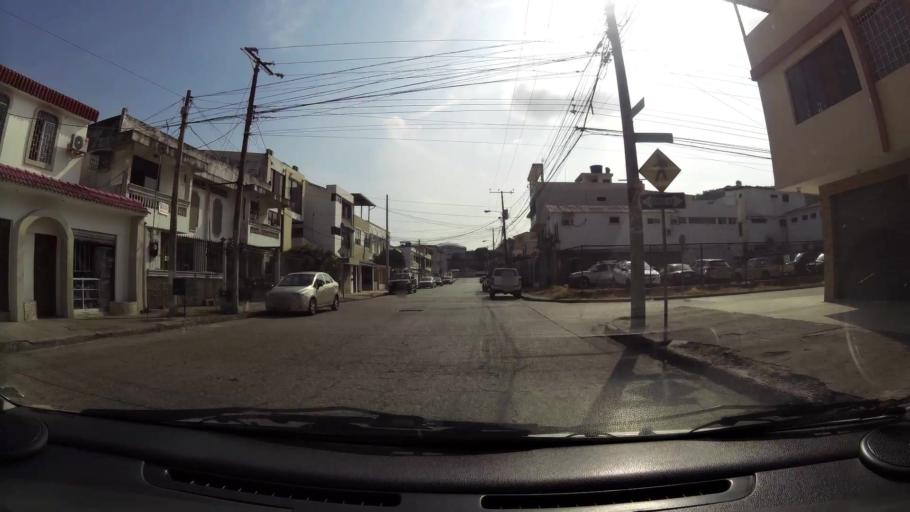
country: EC
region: Guayas
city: Guayaquil
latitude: -2.1819
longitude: -79.9099
